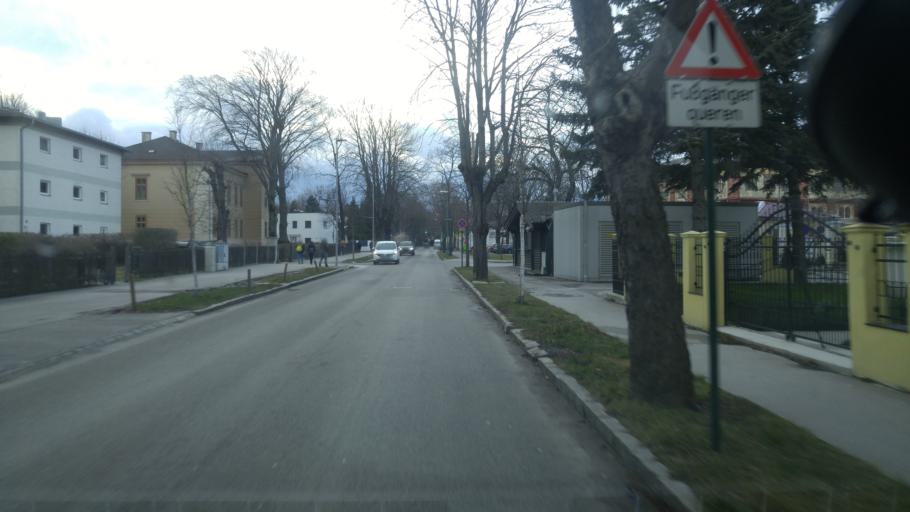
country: AT
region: Lower Austria
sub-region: Politischer Bezirk Baden
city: Bad Voslau
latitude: 47.9685
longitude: 16.2214
